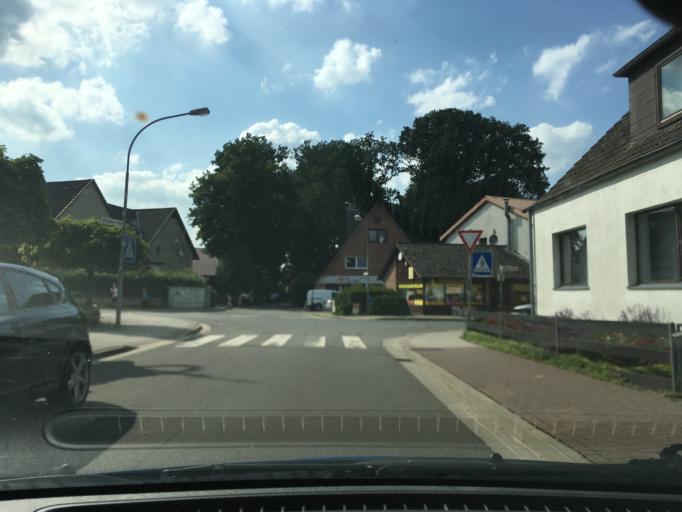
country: DE
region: Lower Saxony
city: Bendestorf
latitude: 53.3684
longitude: 9.9379
